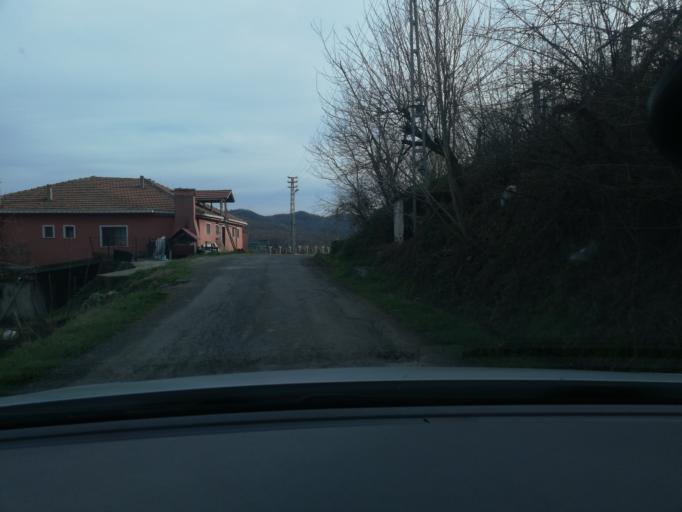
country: TR
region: Zonguldak
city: Kozlu
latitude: 41.3581
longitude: 31.6454
